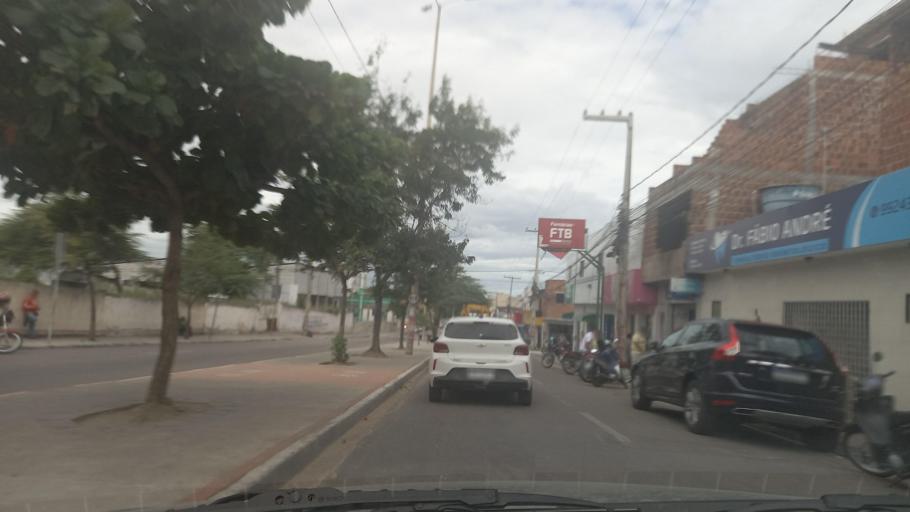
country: BR
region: Pernambuco
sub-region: Caruaru
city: Caruaru
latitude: -8.2747
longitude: -35.9905
